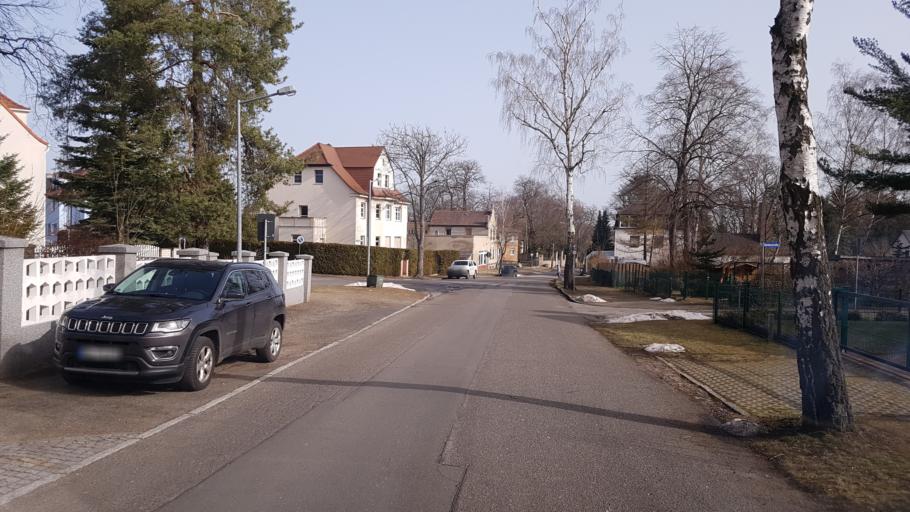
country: DE
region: Brandenburg
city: Lauchhammer
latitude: 51.5035
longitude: 13.7929
